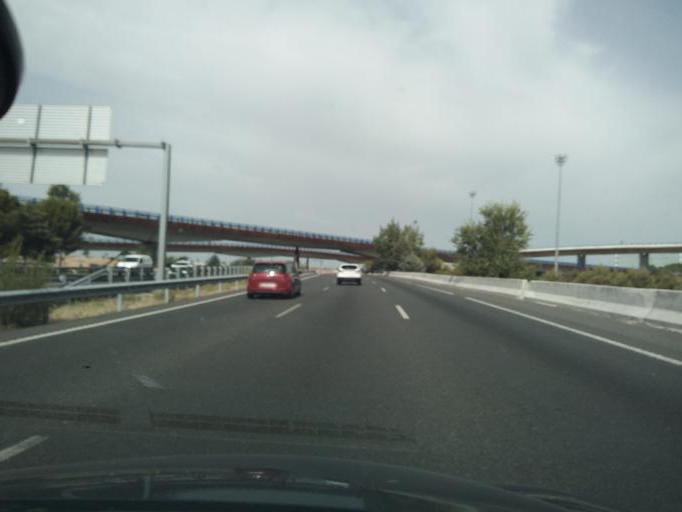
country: ES
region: Madrid
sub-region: Provincia de Madrid
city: Las Tablas
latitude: 40.5094
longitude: -3.6558
